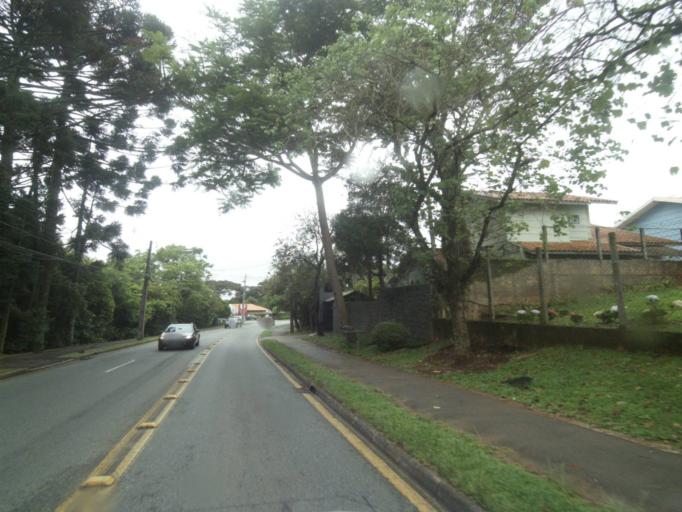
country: BR
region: Parana
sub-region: Curitiba
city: Curitiba
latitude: -25.4223
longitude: -49.3180
